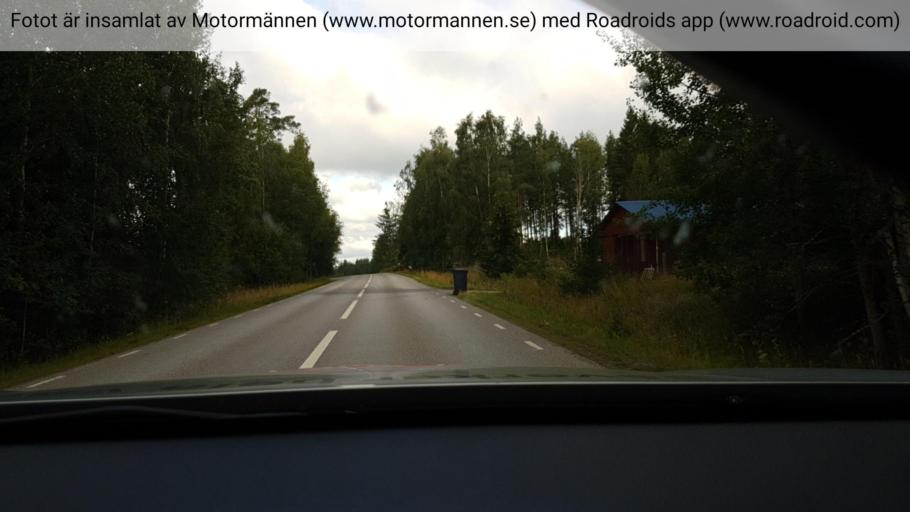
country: SE
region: Stockholm
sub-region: Norrtalje Kommun
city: Nykvarn
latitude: 59.9080
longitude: 18.3012
